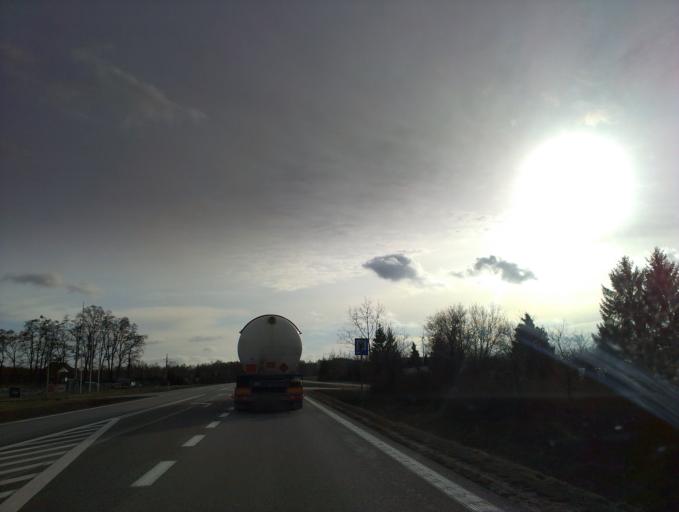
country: PL
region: Kujawsko-Pomorskie
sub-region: Powiat lipnowski
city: Kikol
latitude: 52.9037
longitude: 19.1206
